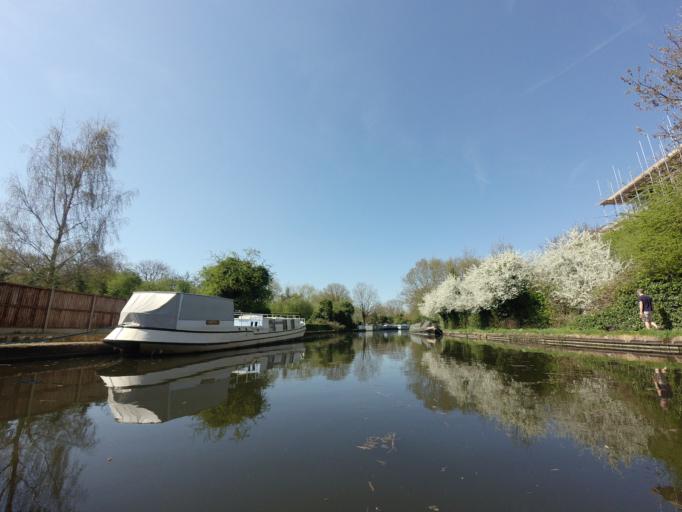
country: GB
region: England
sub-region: Buckinghamshire
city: Iver
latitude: 51.5208
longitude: -0.4837
